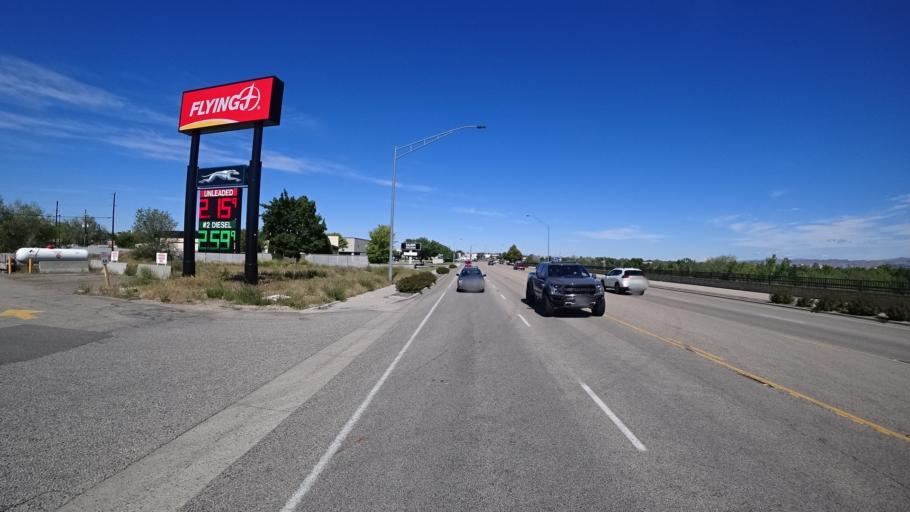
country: US
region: Idaho
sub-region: Ada County
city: Boise
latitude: 43.5721
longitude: -116.1892
